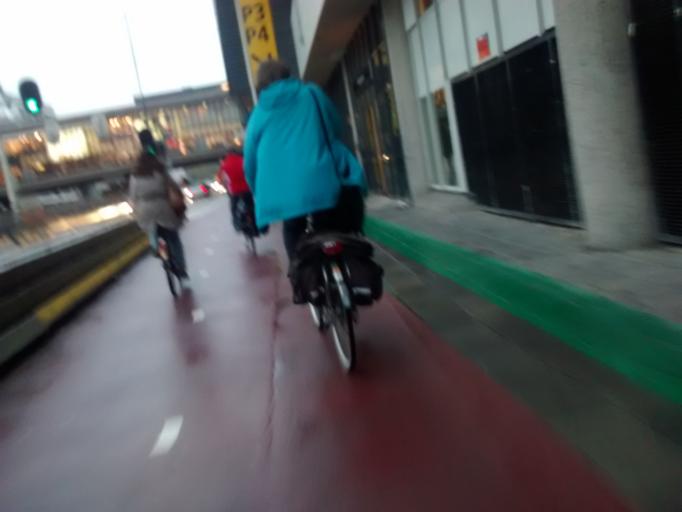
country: NL
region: Utrecht
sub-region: Gemeente Utrecht
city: Utrecht
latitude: 52.0918
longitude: 5.1121
